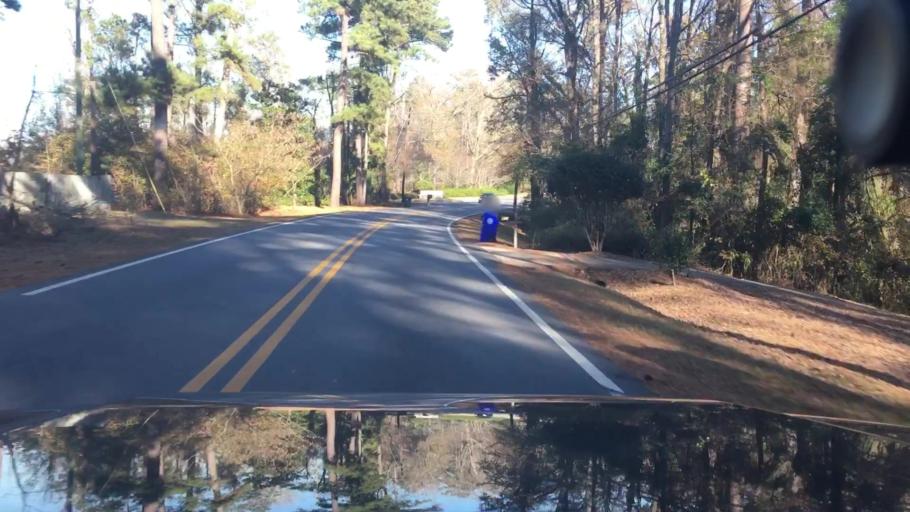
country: US
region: Georgia
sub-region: Bibb County
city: Macon
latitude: 32.8841
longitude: -83.6790
